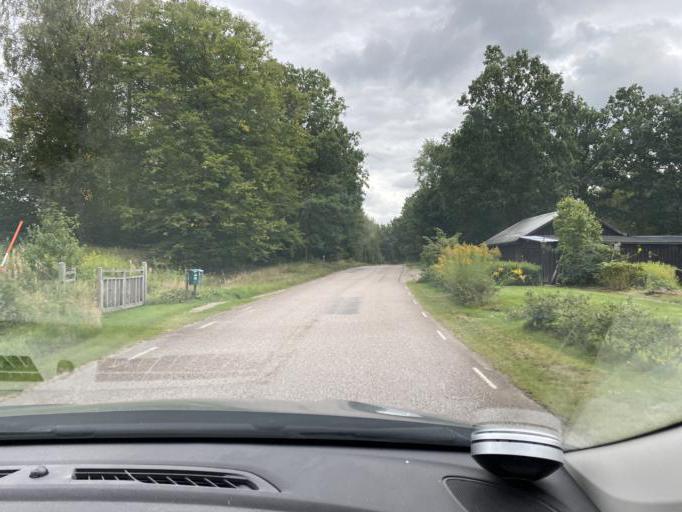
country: SE
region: Kronoberg
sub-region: Markaryds Kommun
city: Markaryd
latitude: 56.4839
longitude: 13.5621
